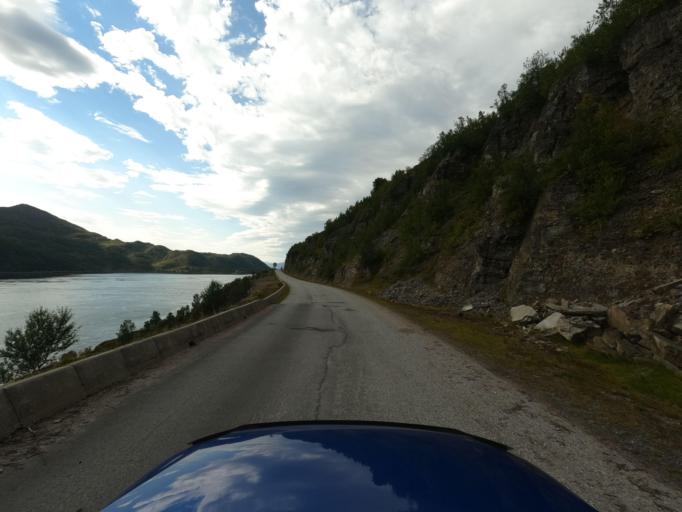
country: NO
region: Finnmark Fylke
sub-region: Kvalsund
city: Kvalsund
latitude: 70.5130
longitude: 23.9289
